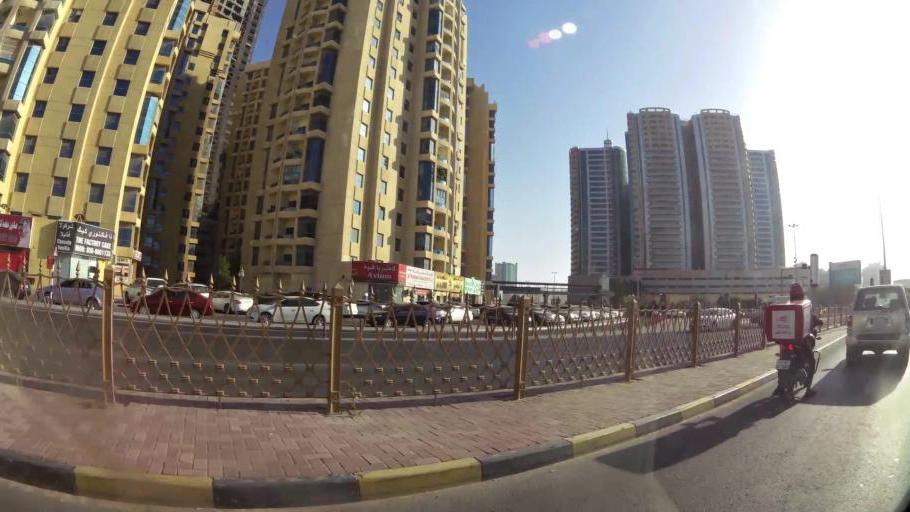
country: AE
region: Ajman
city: Ajman
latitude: 25.3954
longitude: 55.4575
